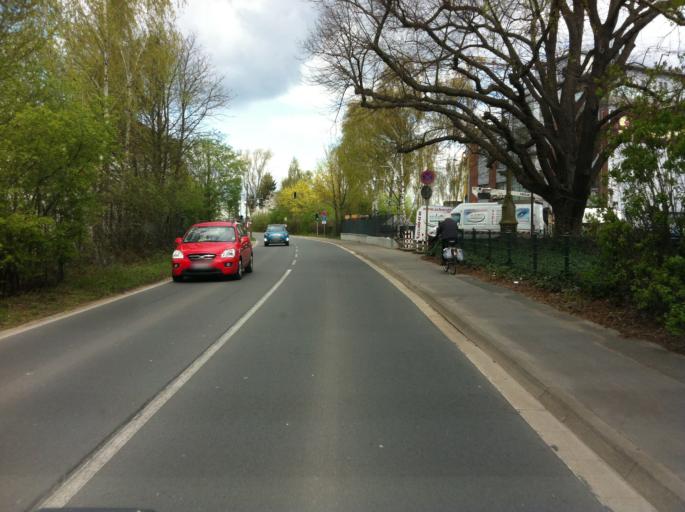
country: DE
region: North Rhine-Westphalia
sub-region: Regierungsbezirk Koln
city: Mengenich
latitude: 51.0061
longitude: 6.8694
